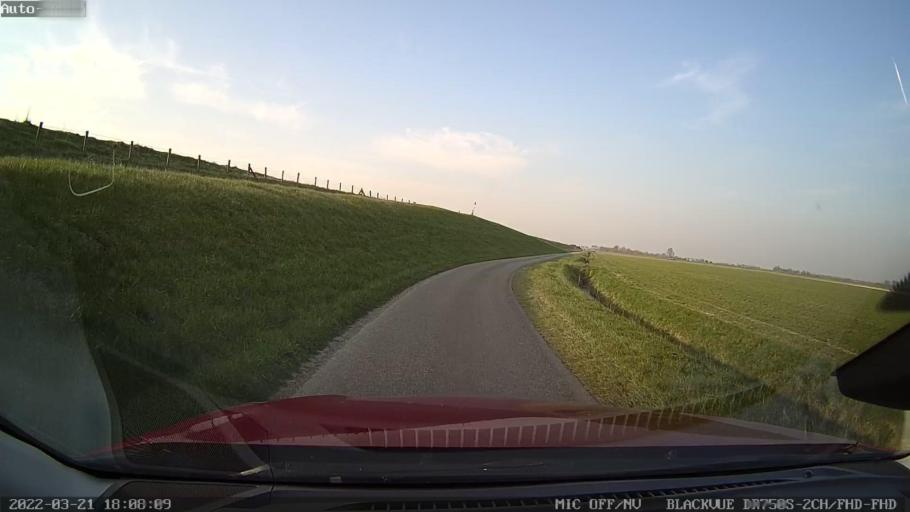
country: NL
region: Zeeland
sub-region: Gemeente Tholen
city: Tholen
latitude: 51.5609
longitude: 4.2341
